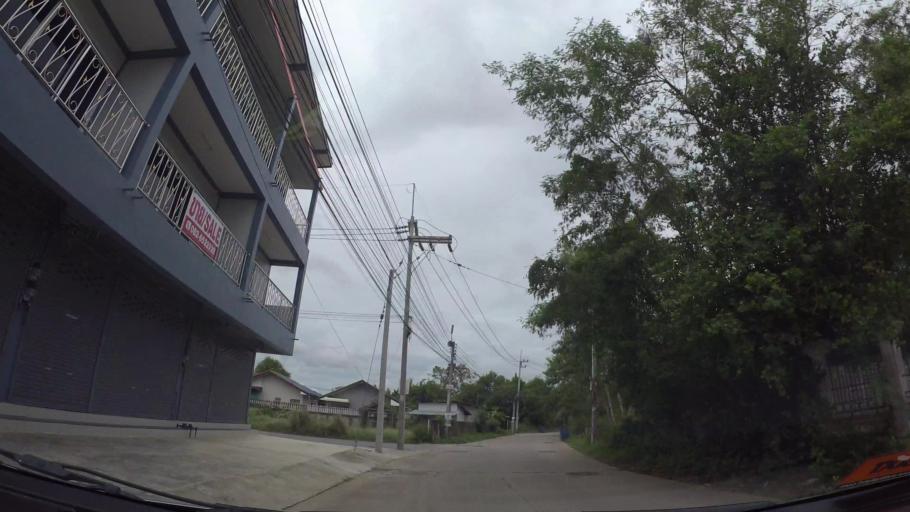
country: TH
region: Chon Buri
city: Sattahip
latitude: 12.7579
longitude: 100.8906
